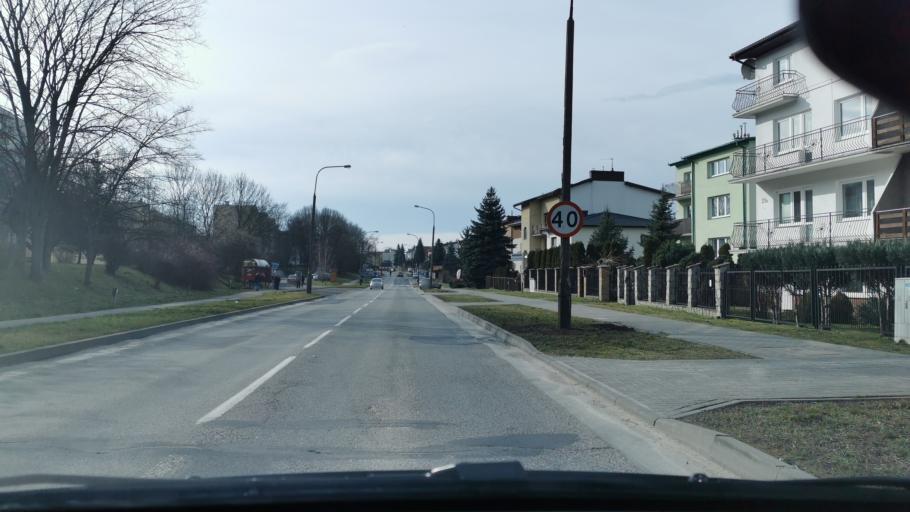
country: PL
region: Lublin Voivodeship
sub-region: Powiat lubelski
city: Lublin
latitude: 51.2115
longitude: 22.5423
